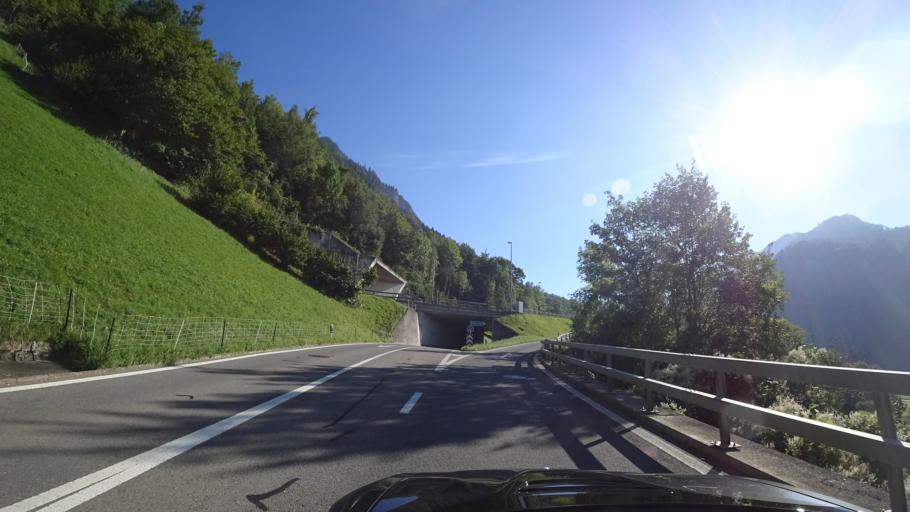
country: CH
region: Obwalden
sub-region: Obwalden
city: Giswil
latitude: 46.8266
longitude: 8.1842
